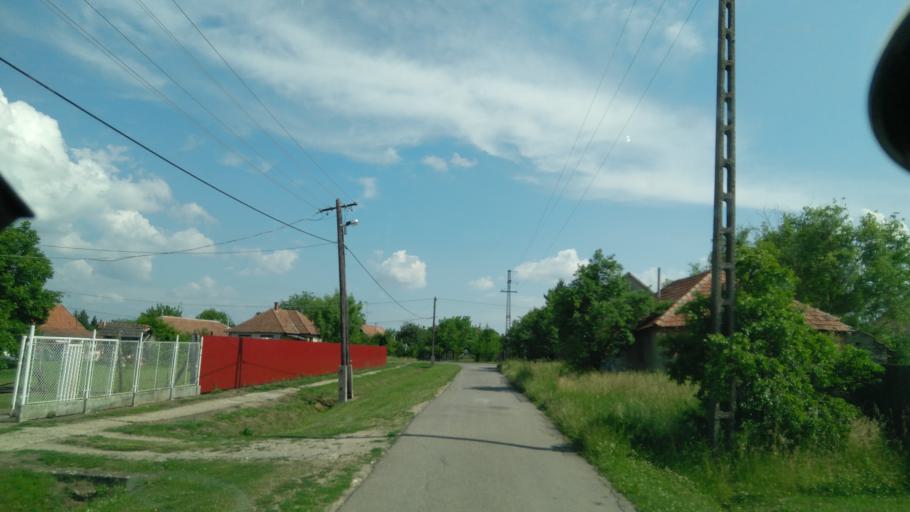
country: HU
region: Bekes
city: Doboz
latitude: 46.7393
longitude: 21.2342
